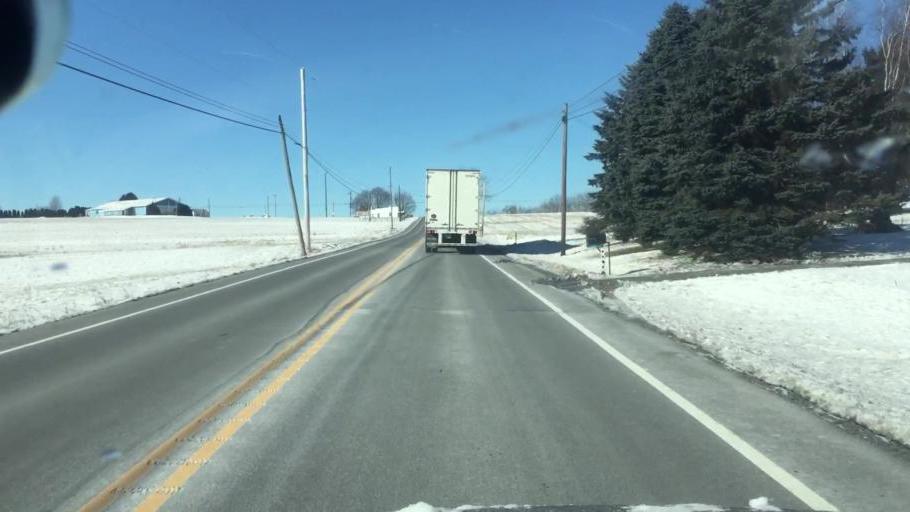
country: US
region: Pennsylvania
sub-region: Luzerne County
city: Nescopeck
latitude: 41.0387
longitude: -76.1377
